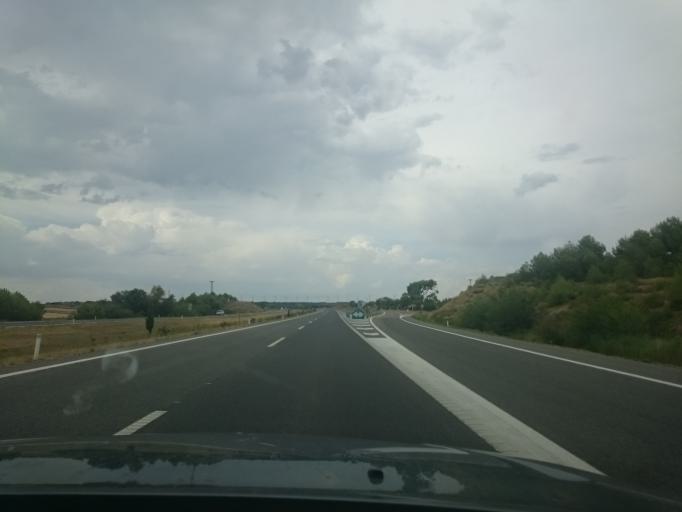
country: ES
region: Navarre
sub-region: Provincia de Navarra
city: Murchante
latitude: 42.0610
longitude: -1.6895
